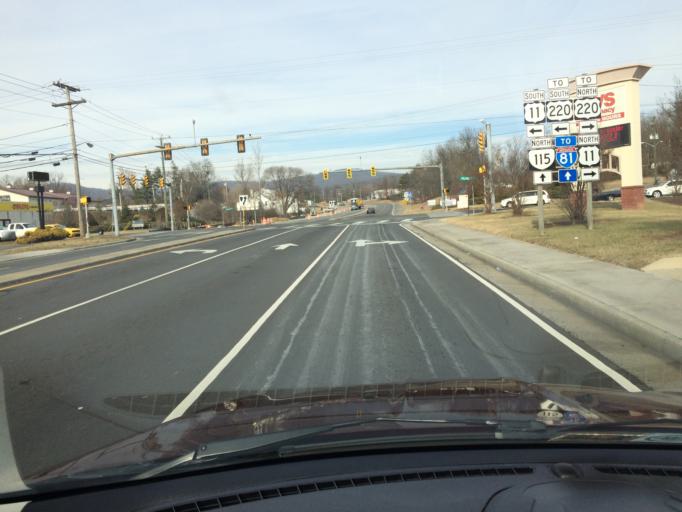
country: US
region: Virginia
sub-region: Roanoke County
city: Hollins
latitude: 37.3472
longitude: -79.9498
